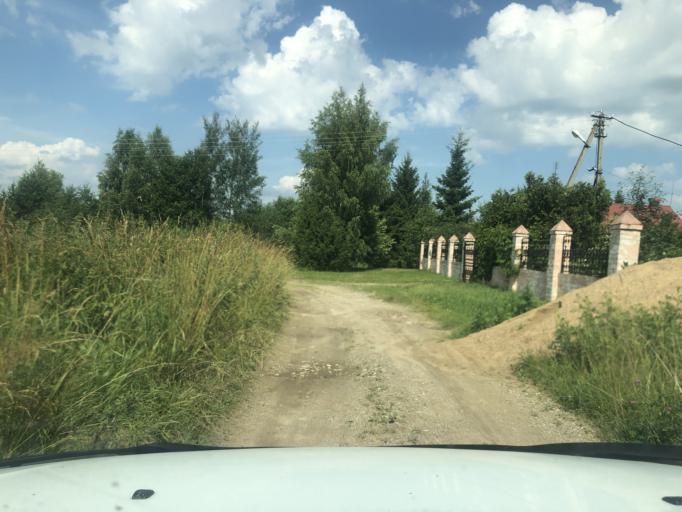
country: RU
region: Jaroslavl
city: Pereslavl'-Zalesskiy
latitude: 57.0454
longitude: 38.8733
